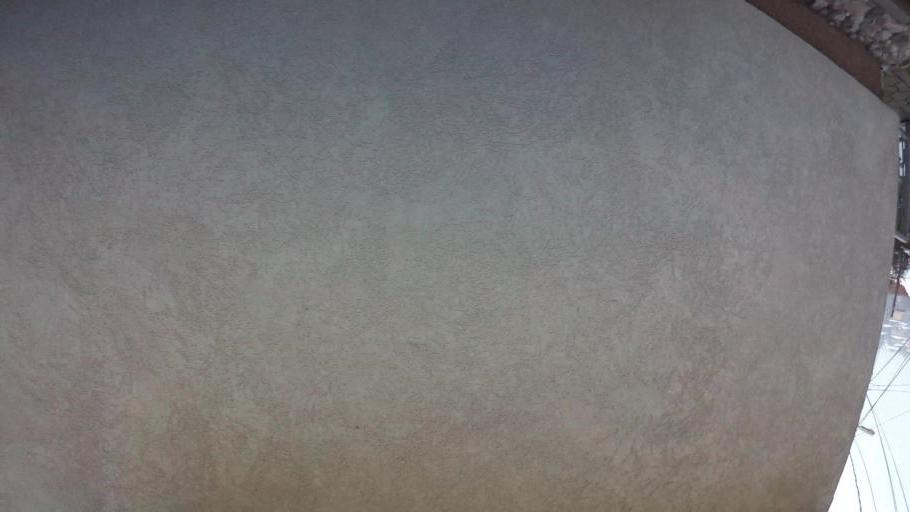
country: BA
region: Federation of Bosnia and Herzegovina
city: Kobilja Glava
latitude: 43.8718
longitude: 18.4001
